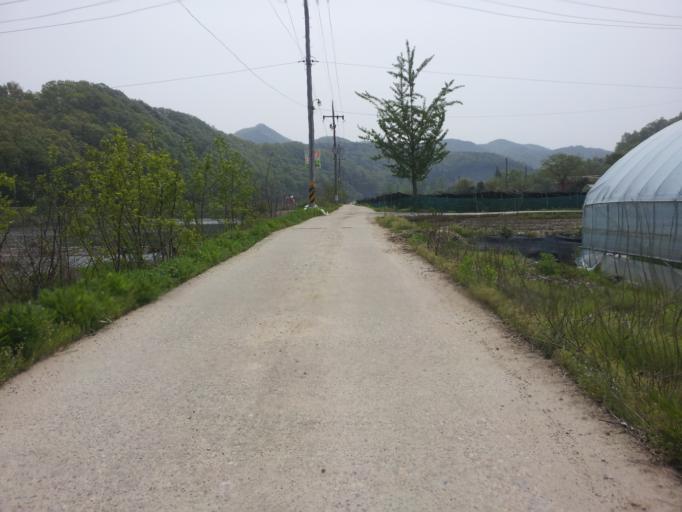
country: KR
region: Daejeon
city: Daejeon
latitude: 36.2703
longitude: 127.3396
